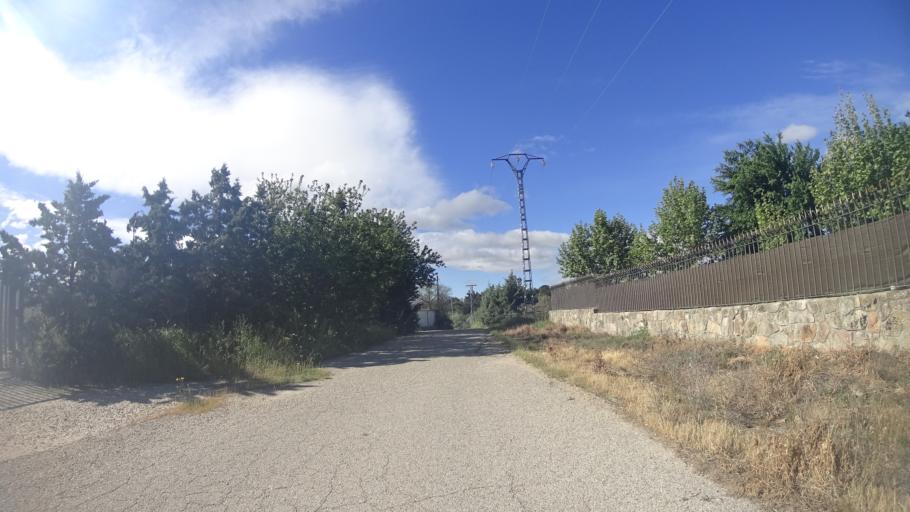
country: ES
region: Madrid
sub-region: Provincia de Madrid
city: Villanueva del Pardillo
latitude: 40.4965
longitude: -3.9406
